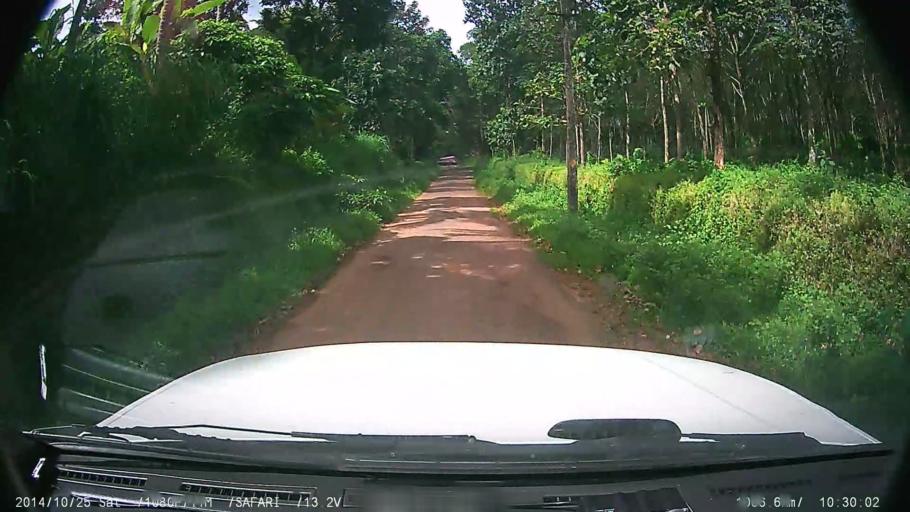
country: IN
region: Kerala
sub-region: Ernakulam
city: Muvattupuzha
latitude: 9.9257
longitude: 76.5695
